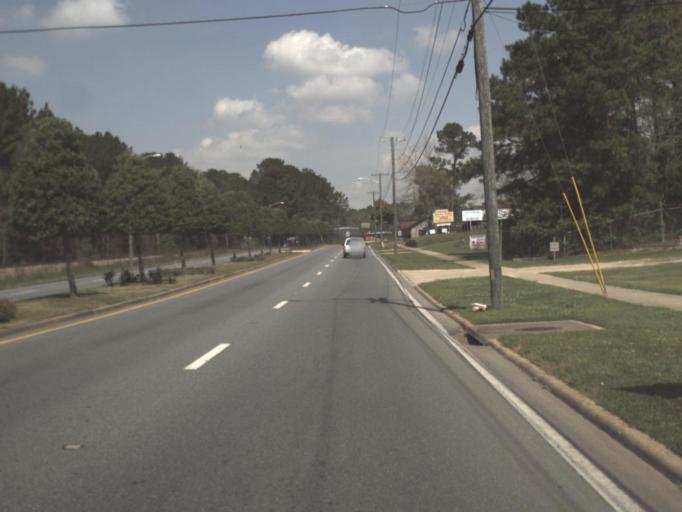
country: US
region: Florida
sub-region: Gadsden County
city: Havana
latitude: 30.6332
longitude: -84.4163
